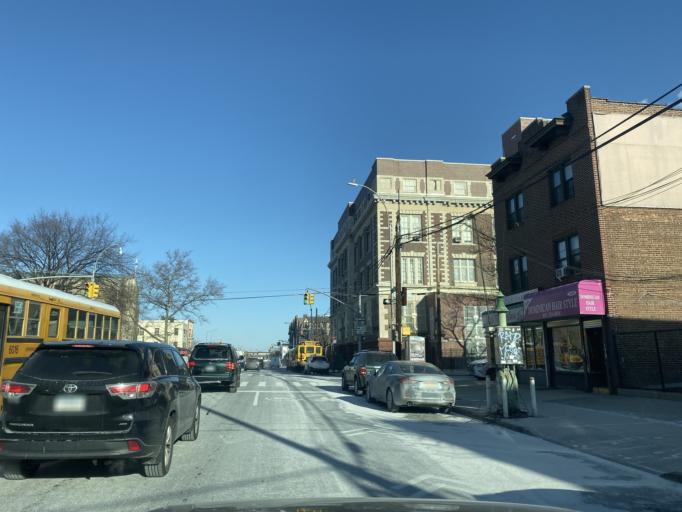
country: US
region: New York
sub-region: Bronx
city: The Bronx
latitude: 40.8288
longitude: -73.8503
